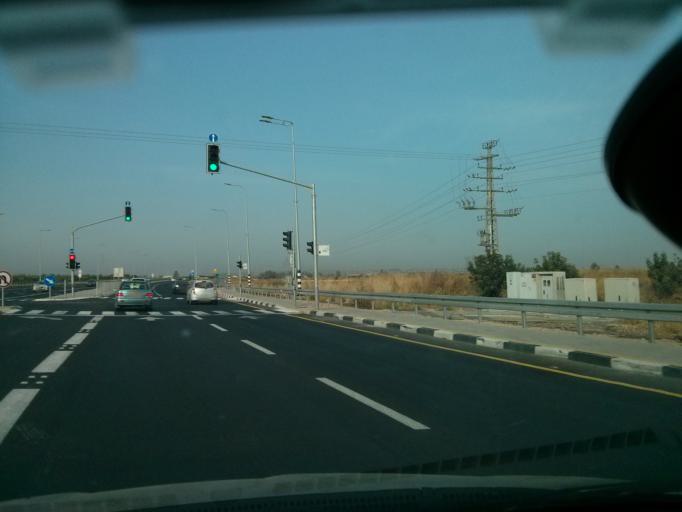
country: IL
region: Central District
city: Bene 'Ayish
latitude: 31.7136
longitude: 34.7360
